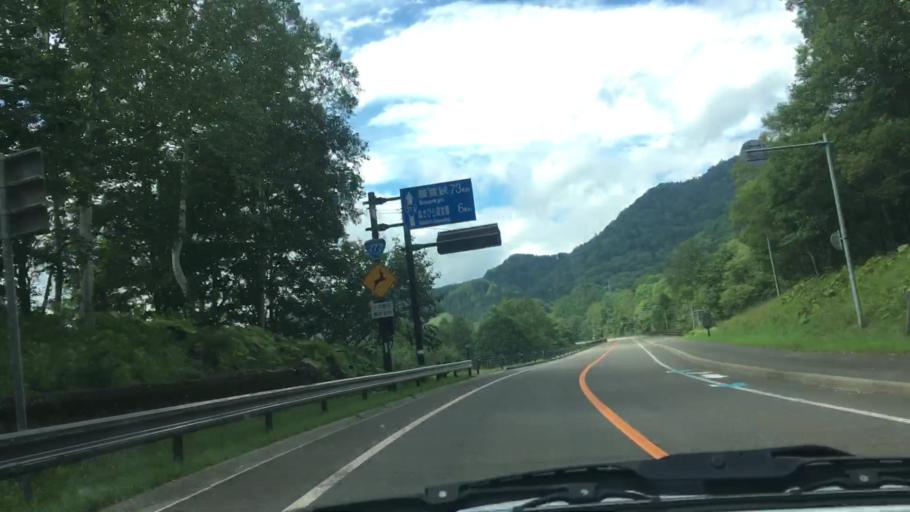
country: JP
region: Hokkaido
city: Otofuke
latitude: 43.3628
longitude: 143.2358
